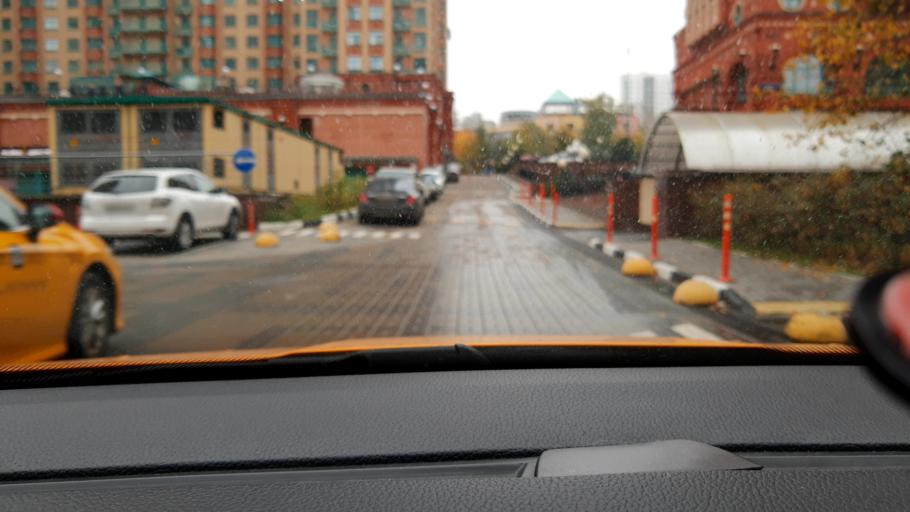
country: RU
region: Moscow
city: Shchukino
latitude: 55.8085
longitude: 37.4493
